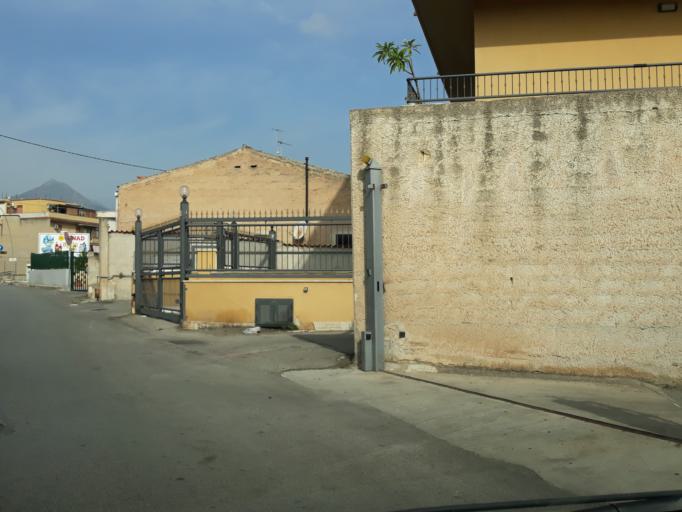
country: IT
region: Sicily
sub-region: Palermo
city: Villa Ciambra
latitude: 38.0866
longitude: 13.3455
